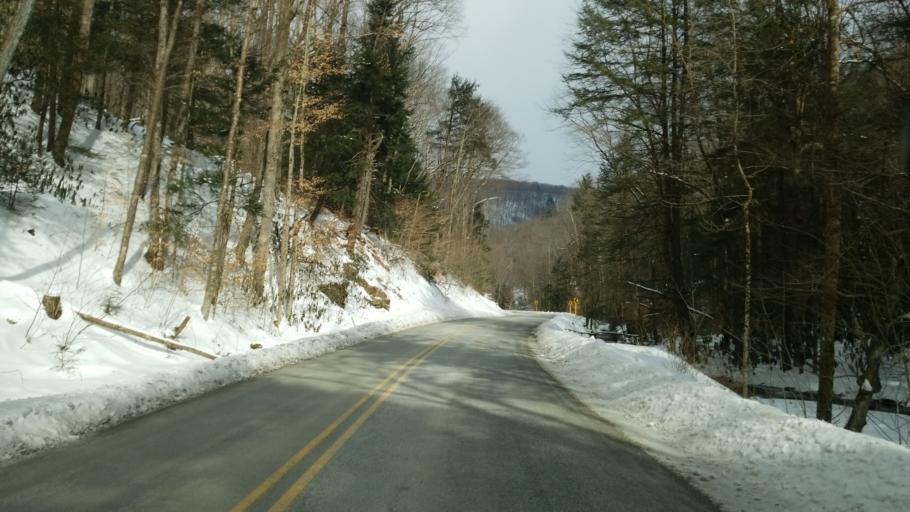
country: US
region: Pennsylvania
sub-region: Clearfield County
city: Shiloh
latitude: 41.2596
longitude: -78.1522
